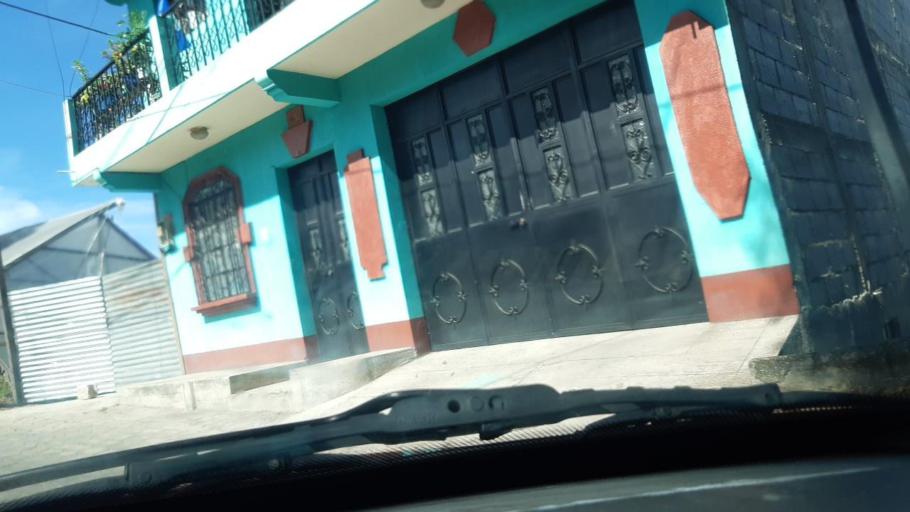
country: GT
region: Quetzaltenango
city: Salcaja
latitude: 14.8868
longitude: -91.4532
